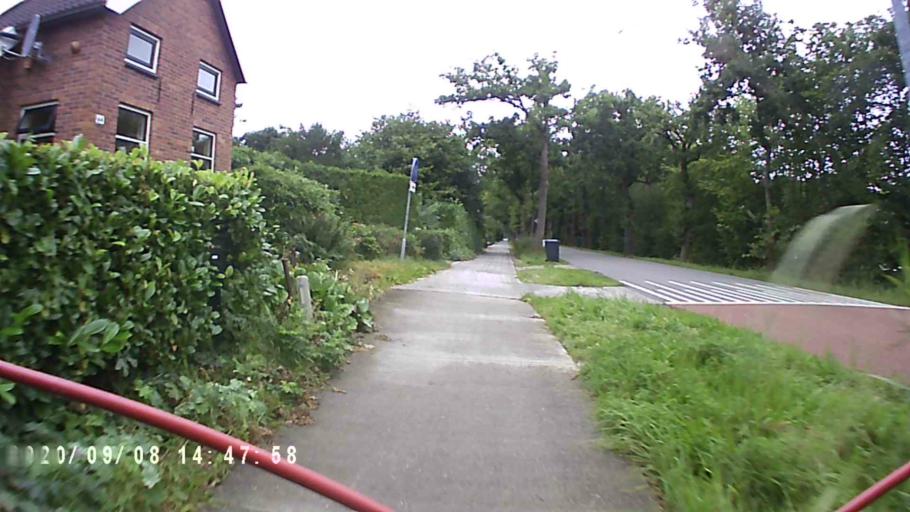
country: NL
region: Groningen
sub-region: Gemeente Slochteren
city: Slochteren
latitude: 53.2379
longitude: 6.8091
